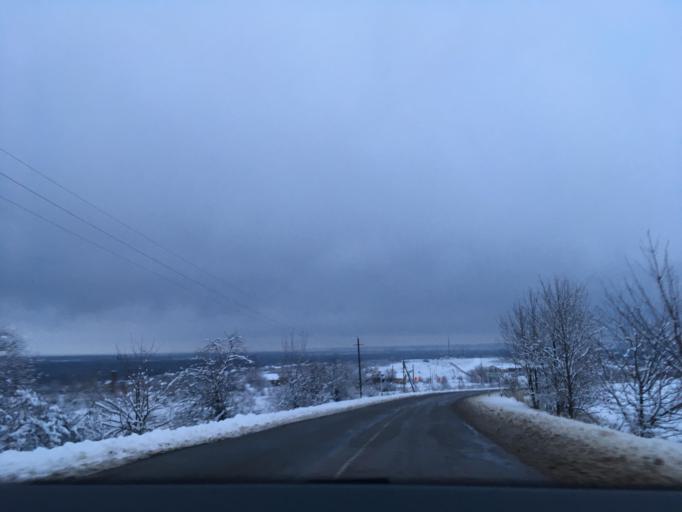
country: RU
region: Voronezj
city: Verkhniy Mamon
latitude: 50.0724
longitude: 40.2902
